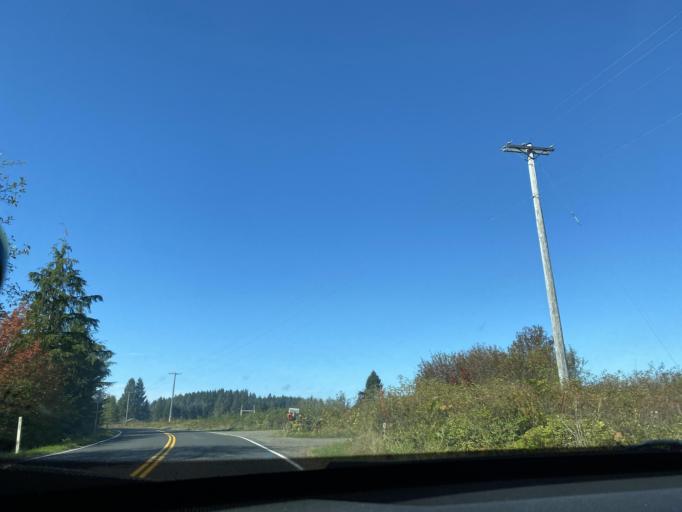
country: US
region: Washington
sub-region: Clallam County
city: Forks
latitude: 47.9489
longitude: -124.5085
